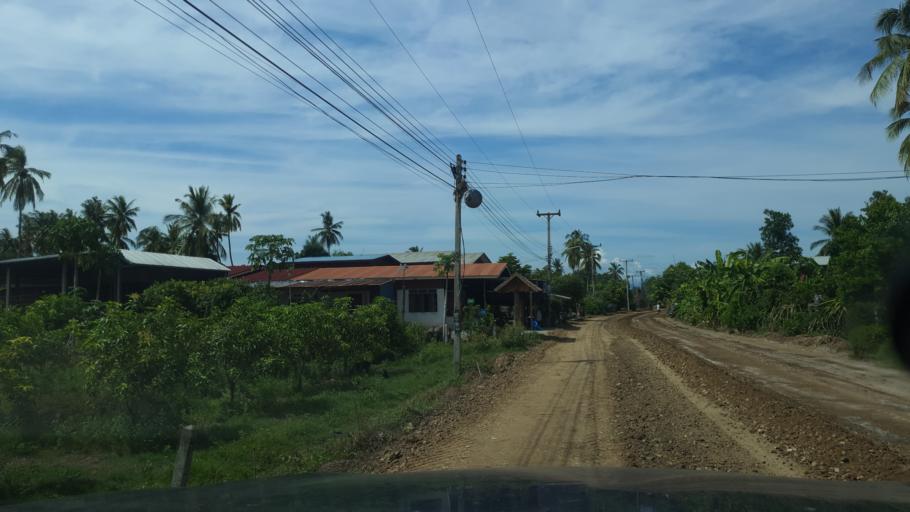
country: TH
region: Sukhothai
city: Si Samrong
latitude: 17.2050
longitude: 99.7207
